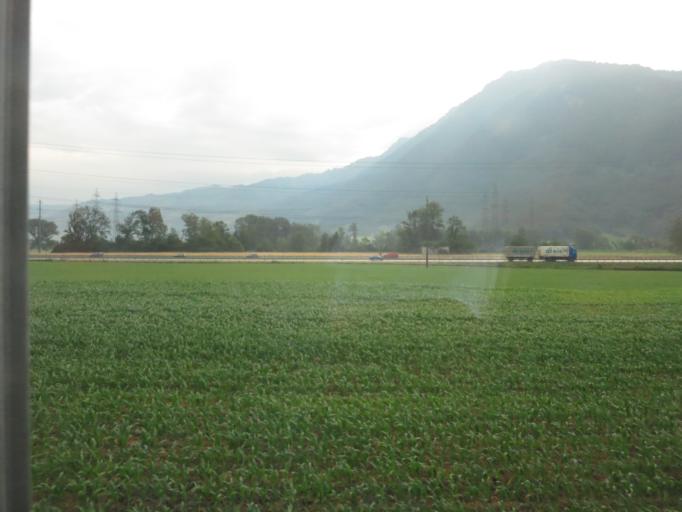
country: CH
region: Glarus
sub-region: Glarus
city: Bilten
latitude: 47.1472
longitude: 9.0387
